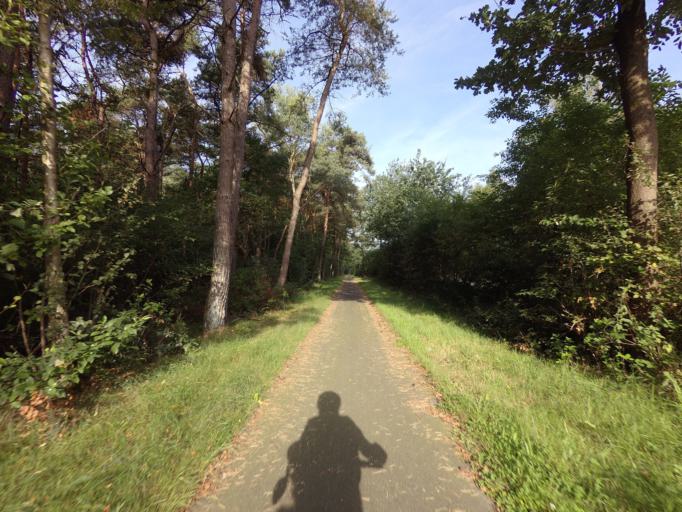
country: DE
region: Lower Saxony
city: Wielen
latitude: 52.5216
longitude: 6.7471
